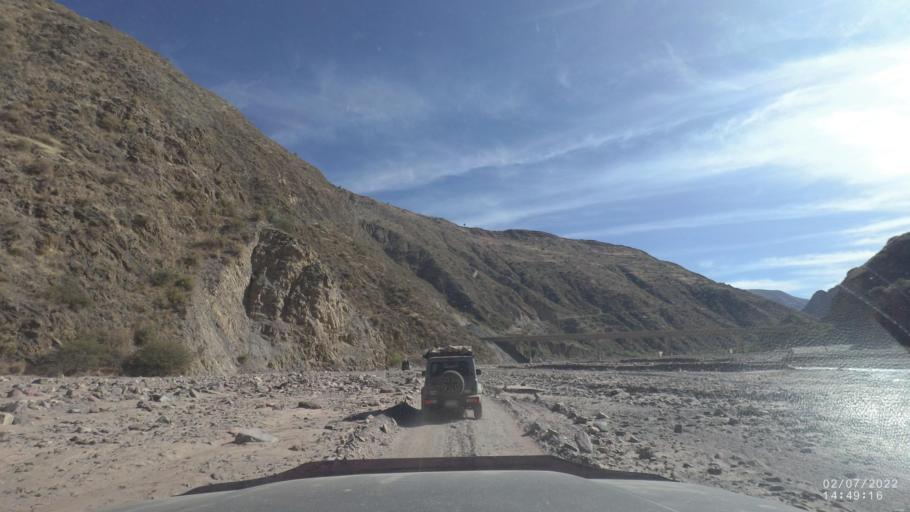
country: BO
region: Cochabamba
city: Irpa Irpa
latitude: -17.8547
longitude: -66.4288
